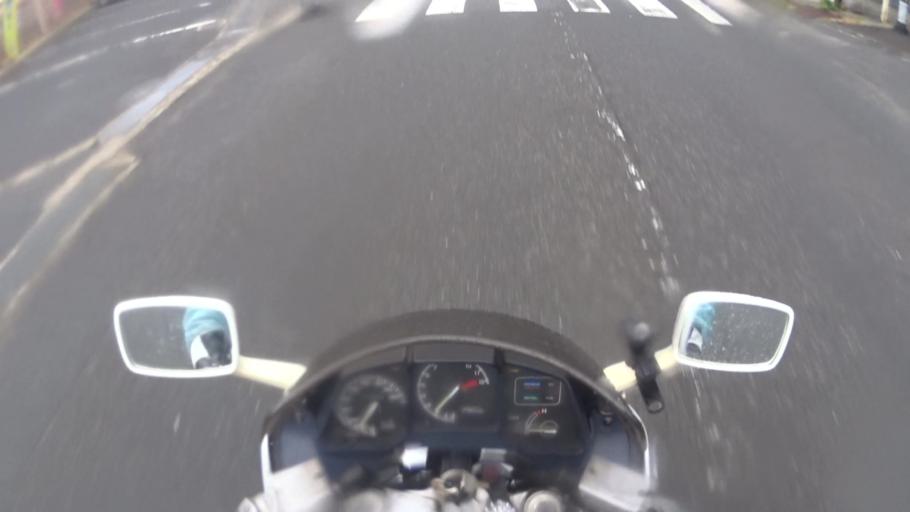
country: JP
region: Kyoto
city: Miyazu
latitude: 35.5480
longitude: 135.2335
